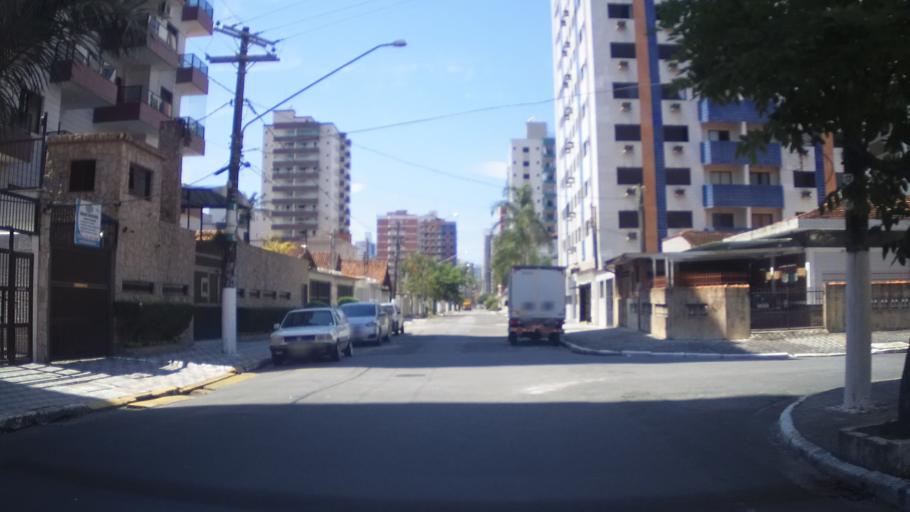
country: BR
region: Sao Paulo
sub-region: Praia Grande
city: Praia Grande
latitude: -24.0227
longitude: -46.4623
